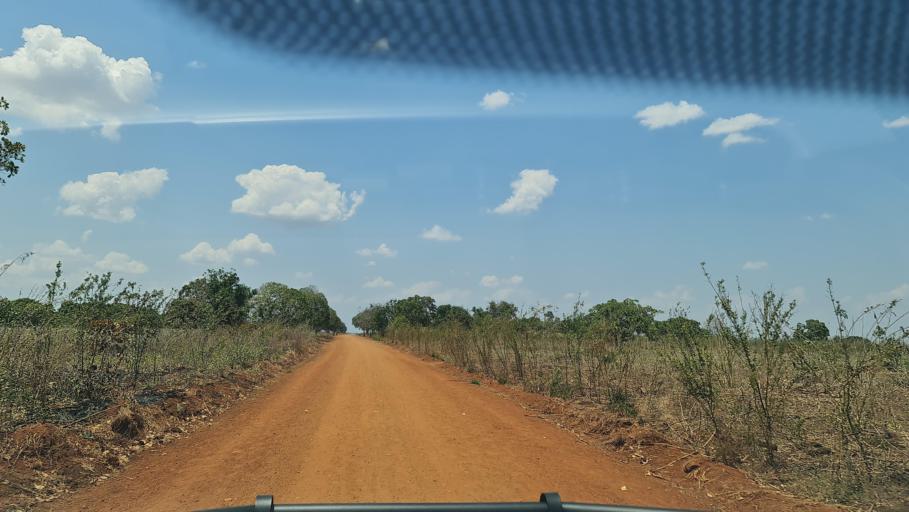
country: MZ
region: Nampula
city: Nacala
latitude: -14.7947
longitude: 40.0679
